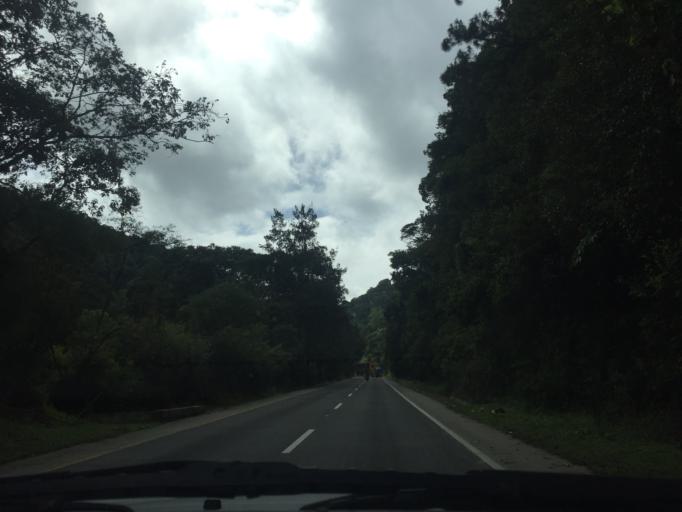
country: GT
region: Sacatepequez
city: Santa Lucia Milpas Altas
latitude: 14.5615
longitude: -90.6933
